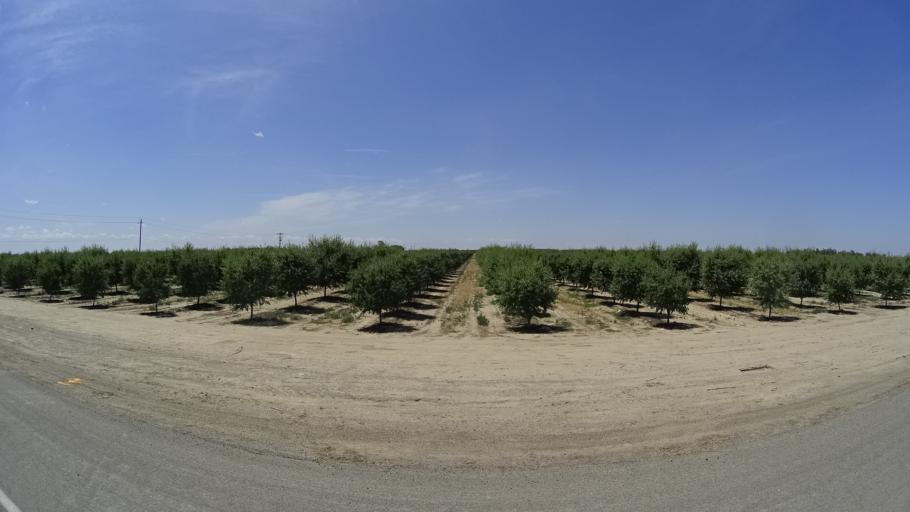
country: US
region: California
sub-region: Kings County
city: Home Garden
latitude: 36.2703
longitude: -119.6550
